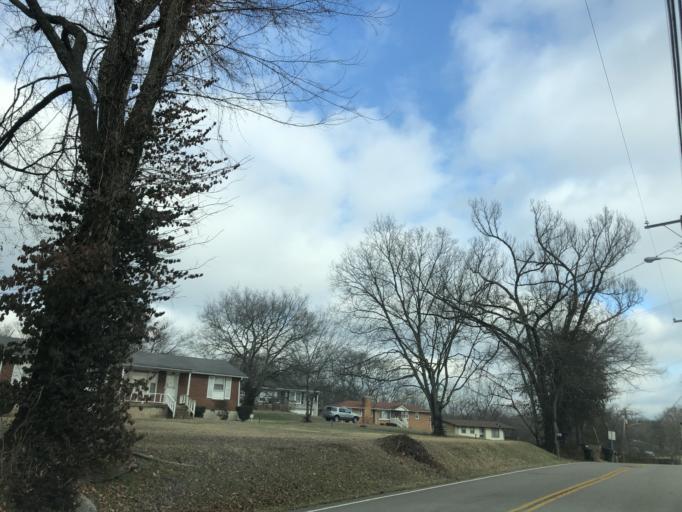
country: US
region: Tennessee
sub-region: Davidson County
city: Nashville
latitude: 36.2048
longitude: -86.8011
